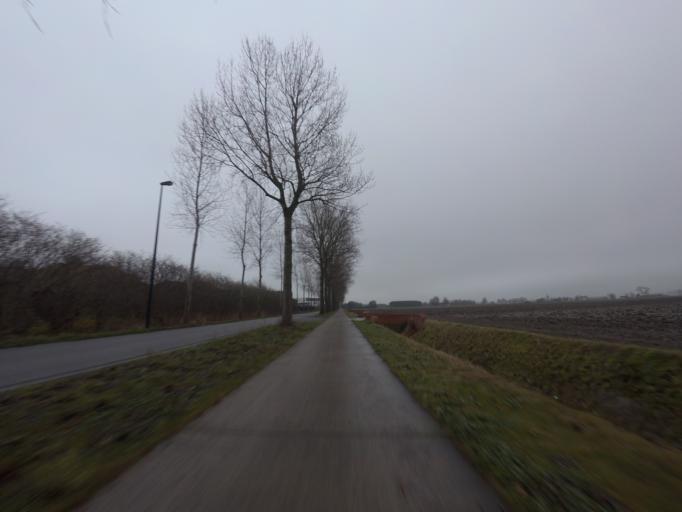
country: BE
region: Flanders
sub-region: Provincie West-Vlaanderen
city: Knokke-Heist
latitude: 51.3184
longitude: 3.2892
